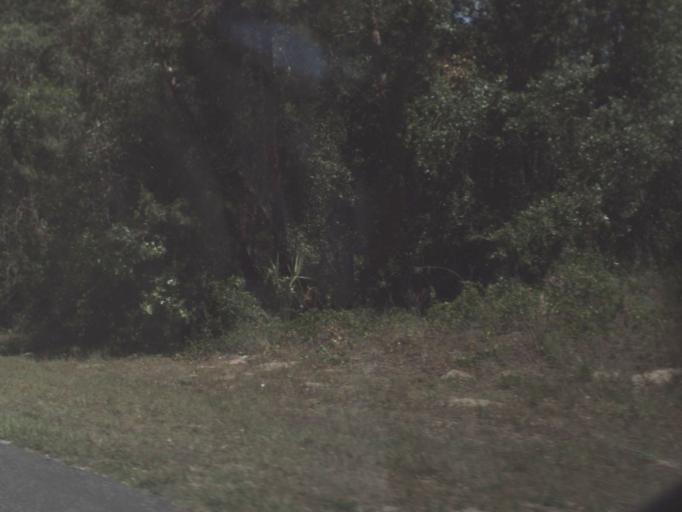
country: US
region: Florida
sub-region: Marion County
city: Silver Springs Shores
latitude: 29.2033
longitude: -81.9374
